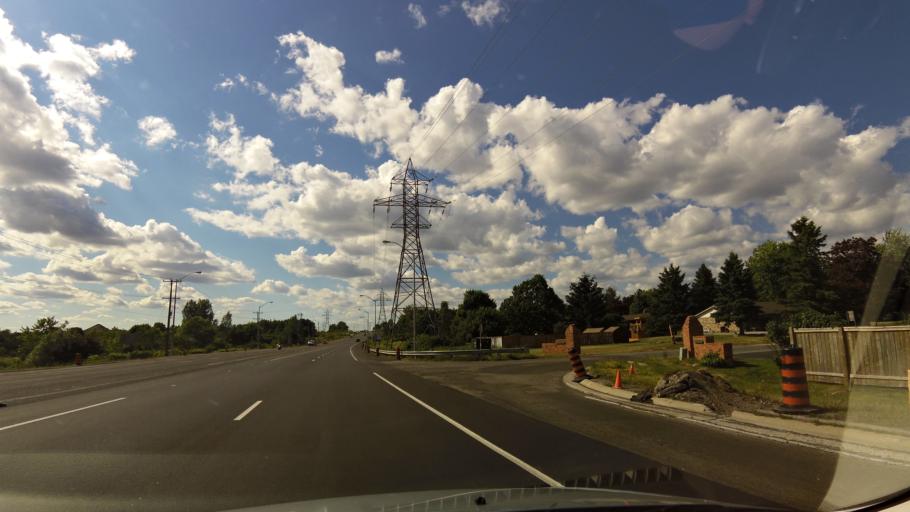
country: CA
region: Ontario
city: Ancaster
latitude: 43.3939
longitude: -80.0287
